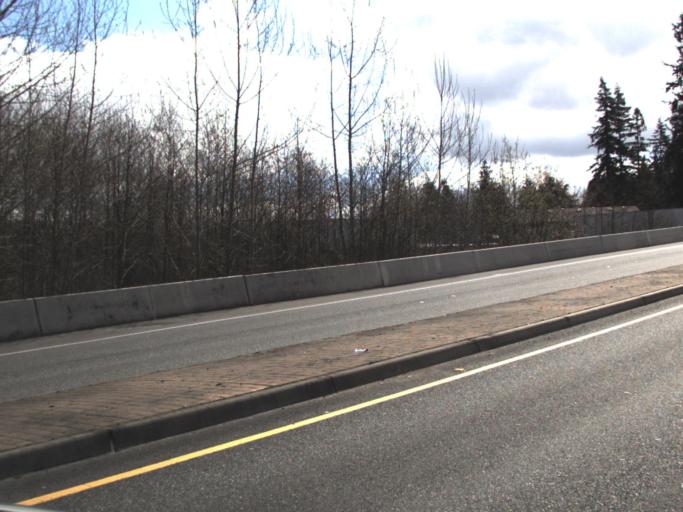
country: US
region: Washington
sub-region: Pierce County
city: Edgewood
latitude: 47.2594
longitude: -122.2961
